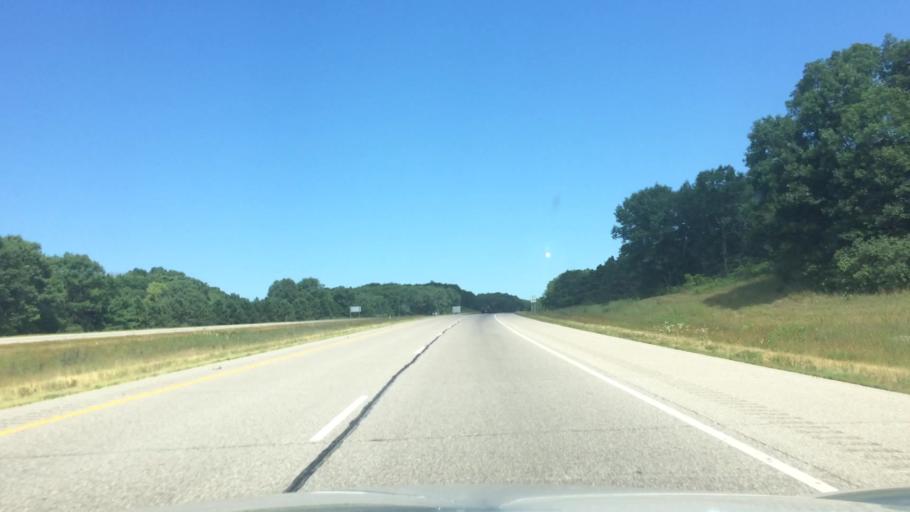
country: US
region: Wisconsin
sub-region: Marquette County
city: Westfield
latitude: 44.0425
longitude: -89.5355
